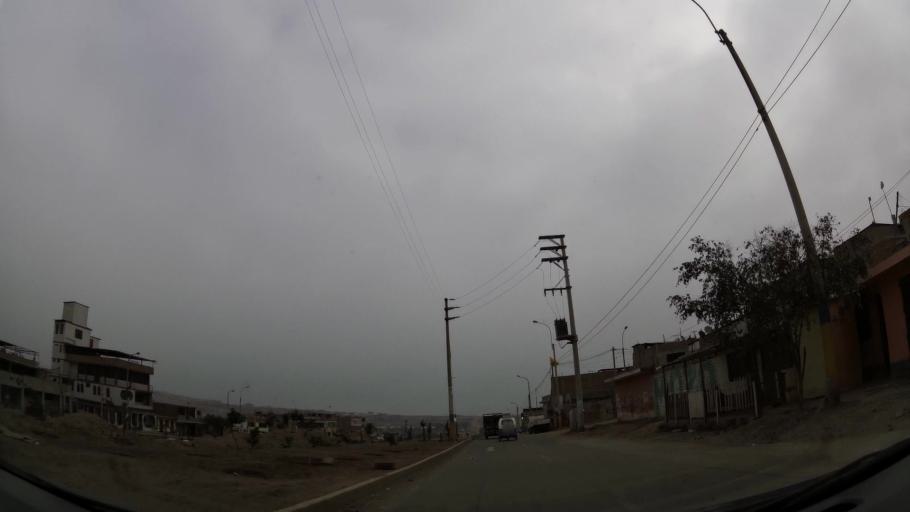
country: PE
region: Lima
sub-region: Lima
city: Surco
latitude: -12.2149
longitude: -76.9517
